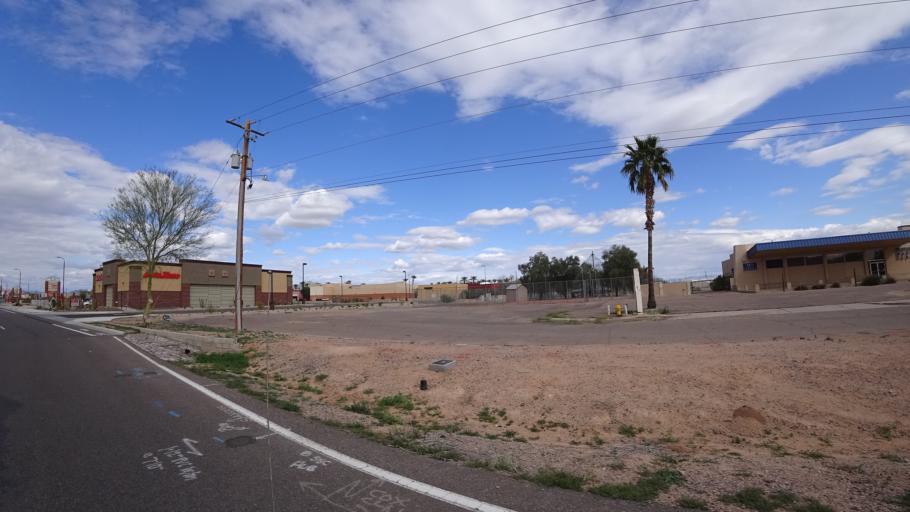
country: US
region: Arizona
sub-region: Maricopa County
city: Scottsdale
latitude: 33.5357
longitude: -111.8915
